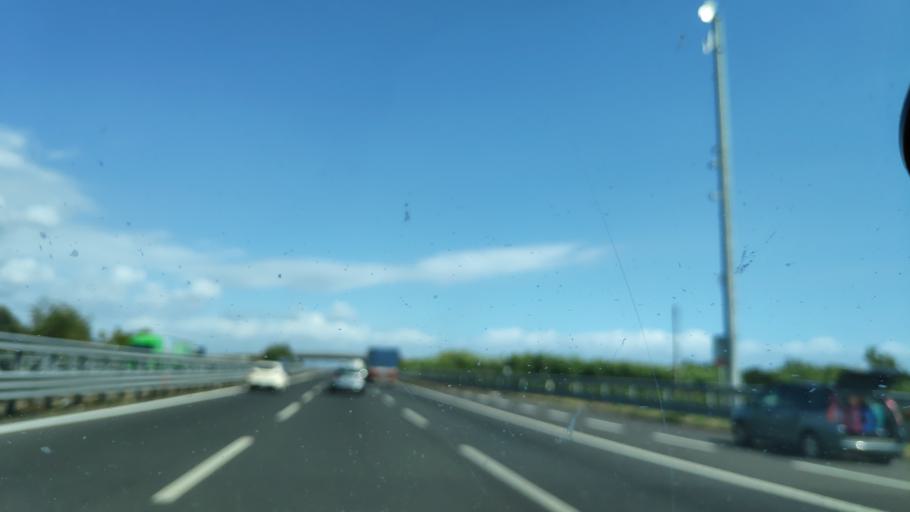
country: IT
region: Campania
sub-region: Provincia di Salerno
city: Pontecagnano
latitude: 40.6477
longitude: 14.8844
